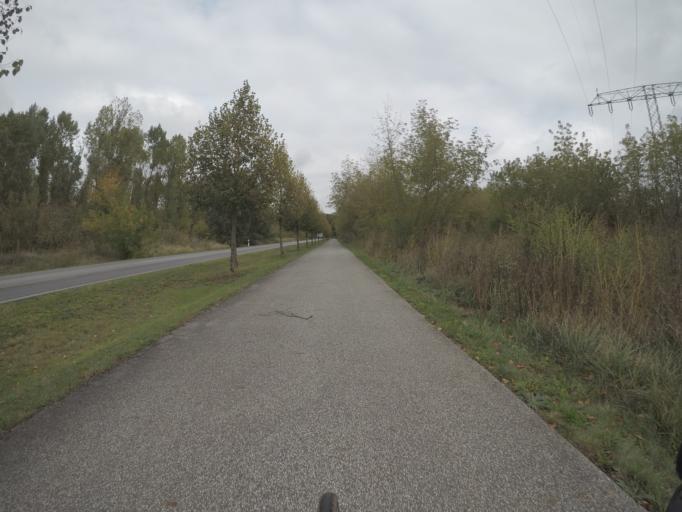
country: DE
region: Berlin
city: Buch
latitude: 52.6756
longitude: 13.5023
